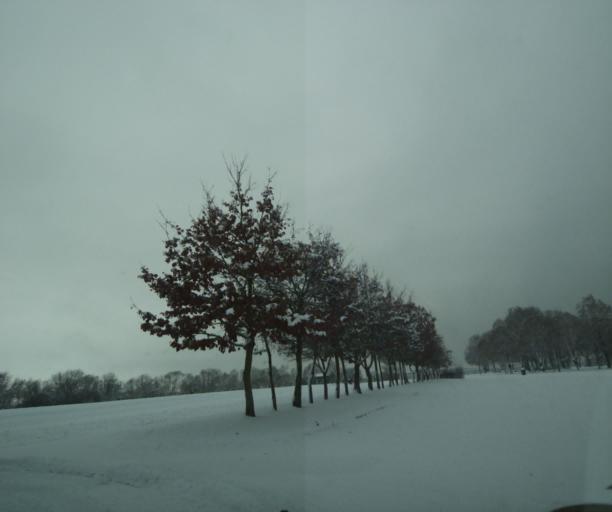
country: FR
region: Champagne-Ardenne
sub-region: Departement de la Haute-Marne
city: Montier-en-Der
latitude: 48.5577
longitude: 4.7902
